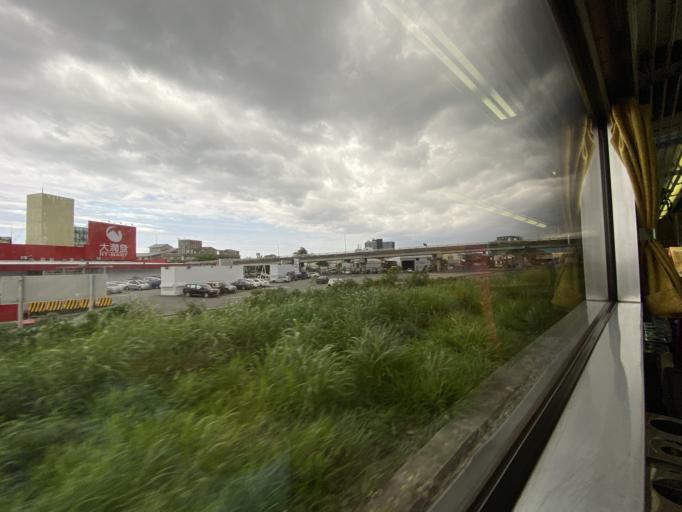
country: TW
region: Taiwan
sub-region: Taitung
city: Taitung
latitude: 22.7734
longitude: 121.1058
